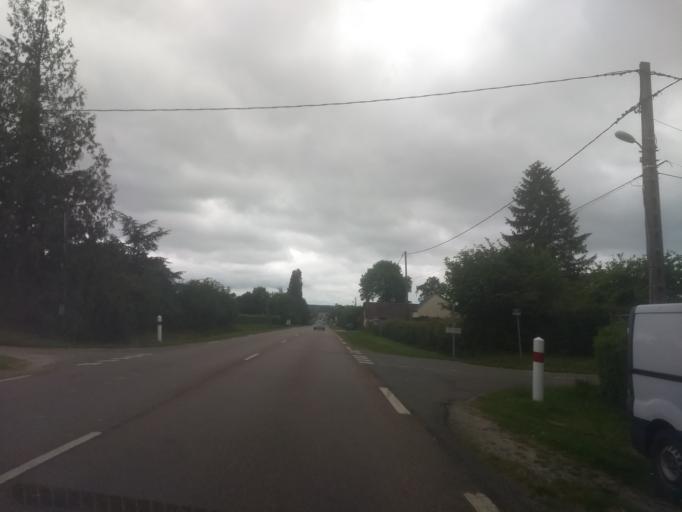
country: FR
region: Centre
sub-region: Departement d'Eure-et-Loir
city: Chateauneuf-en-Thymerais
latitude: 48.5408
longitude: 1.1629
